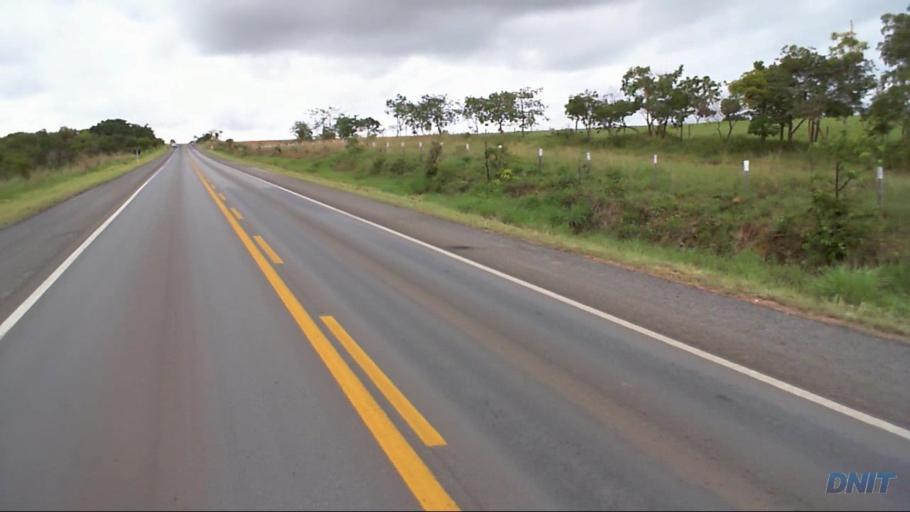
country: BR
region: Goias
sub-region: Padre Bernardo
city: Padre Bernardo
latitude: -15.2153
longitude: -48.5957
